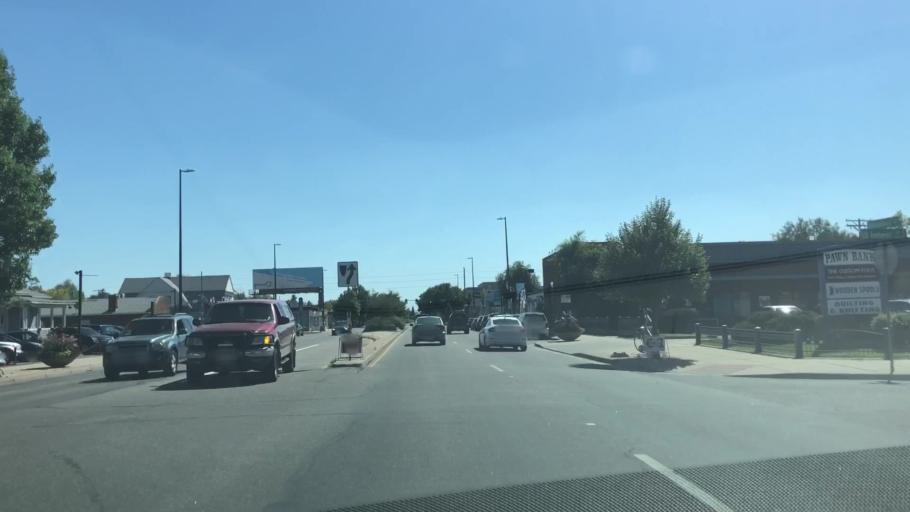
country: US
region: Colorado
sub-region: Arapahoe County
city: Englewood
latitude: 39.6659
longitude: -104.9876
